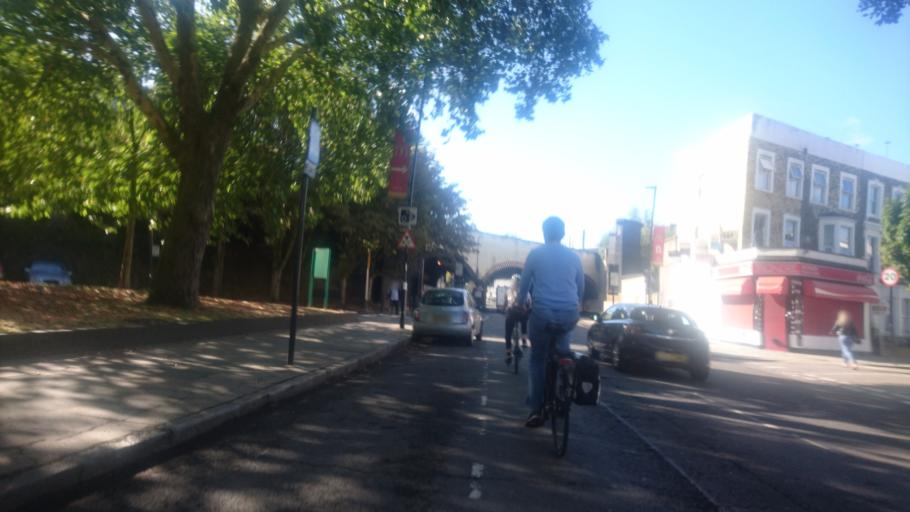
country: GB
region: England
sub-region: Greater London
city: Holloway
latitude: 51.5558
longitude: -0.1113
